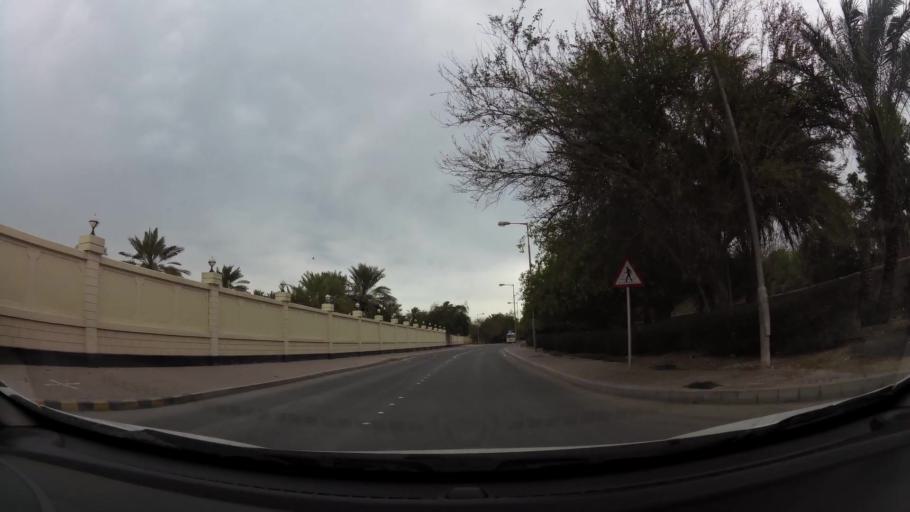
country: BH
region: Central Governorate
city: Madinat Hamad
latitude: 26.1506
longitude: 50.4546
